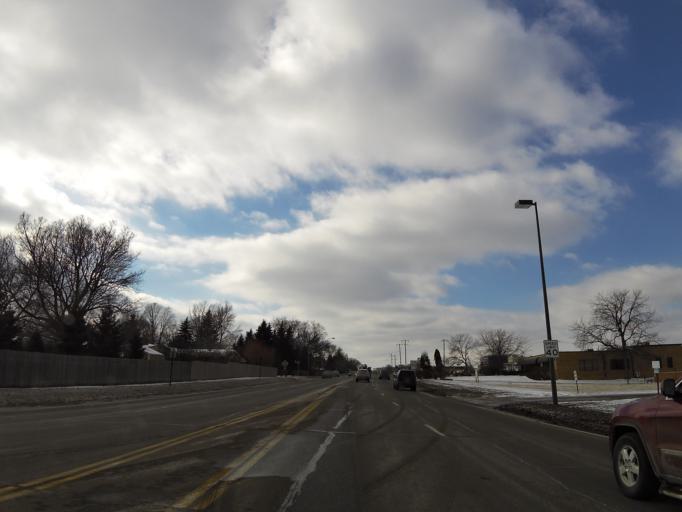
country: US
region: Minnesota
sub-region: Hennepin County
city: Saint Louis Park
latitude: 44.9262
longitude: -93.3769
